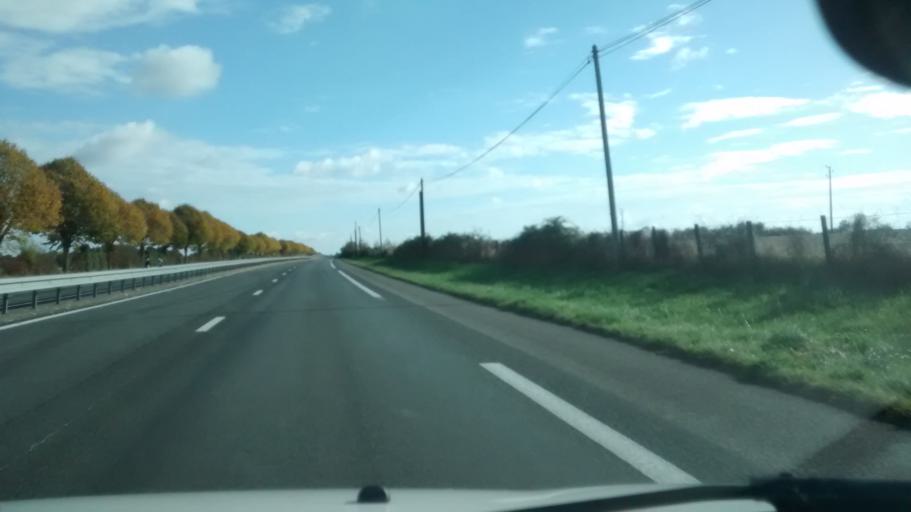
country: FR
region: Pays de la Loire
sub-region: Departement de Maine-et-Loire
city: Pouance
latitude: 47.7342
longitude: -1.1353
